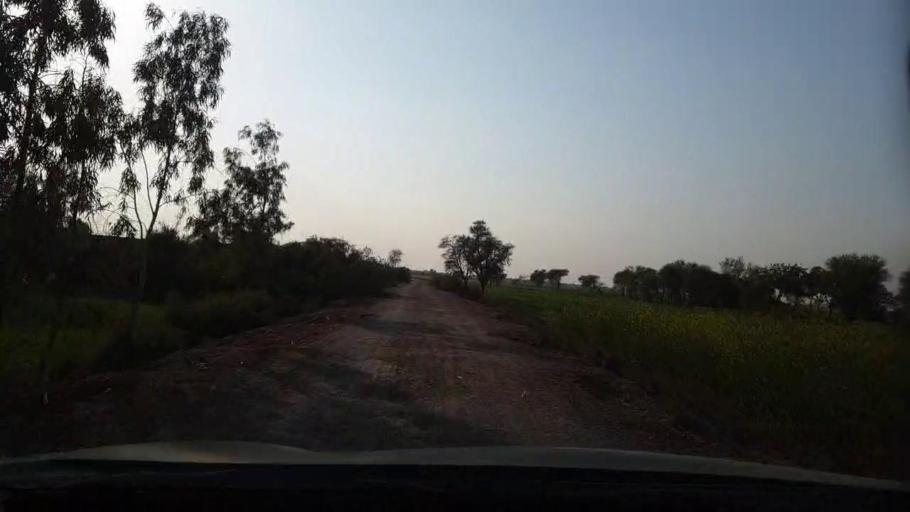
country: PK
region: Sindh
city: Berani
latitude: 25.6511
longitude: 68.8079
